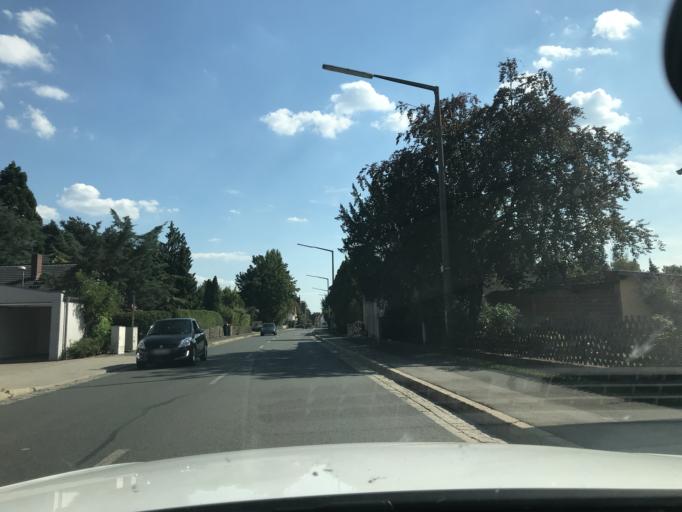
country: DE
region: Bavaria
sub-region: Regierungsbezirk Mittelfranken
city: Erlangen
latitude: 49.5565
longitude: 10.9883
